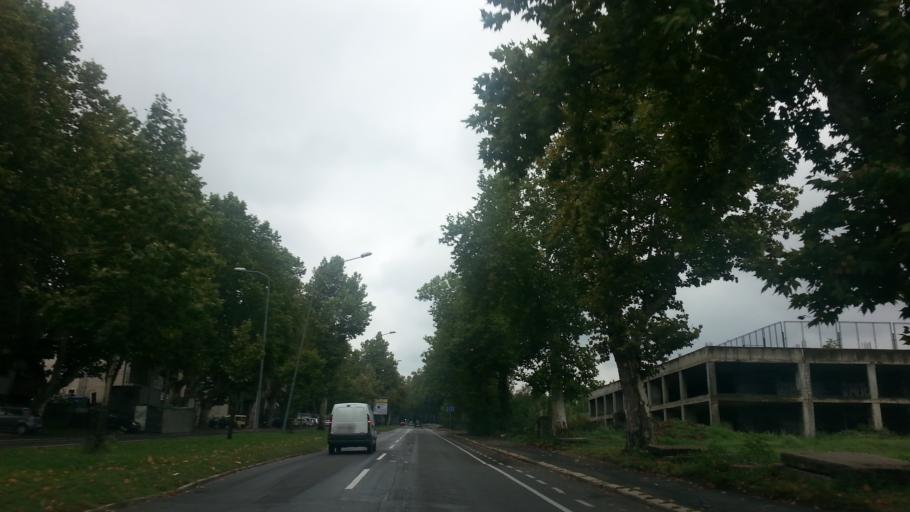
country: RS
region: Central Serbia
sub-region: Belgrade
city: Vozdovac
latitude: 44.7827
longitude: 20.4669
